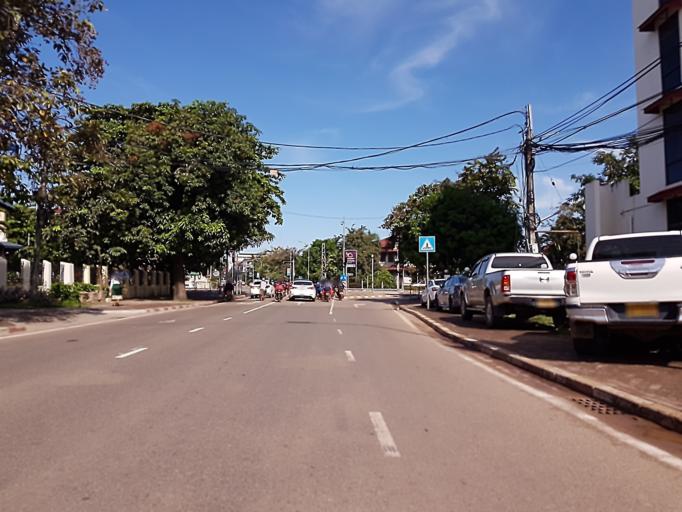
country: LA
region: Vientiane
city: Vientiane
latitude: 17.9639
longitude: 102.6126
